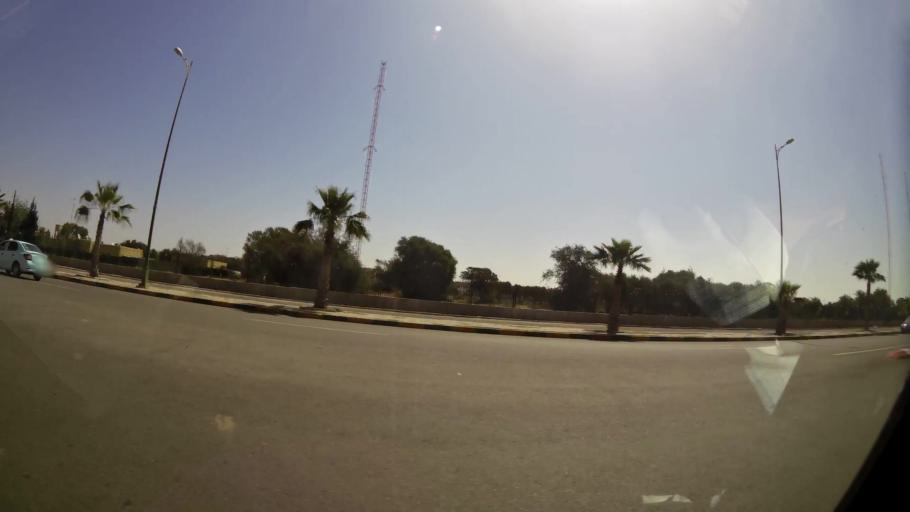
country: MA
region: Souss-Massa-Draa
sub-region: Inezgane-Ait Mellou
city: Inezgane
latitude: 30.3294
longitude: -9.5038
